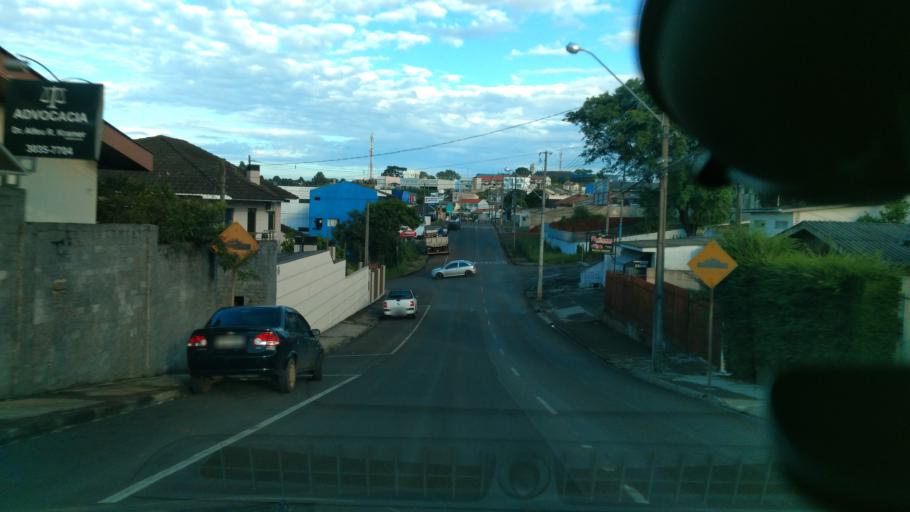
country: BR
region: Parana
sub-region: Guarapuava
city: Guarapuava
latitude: -25.3825
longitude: -51.4737
